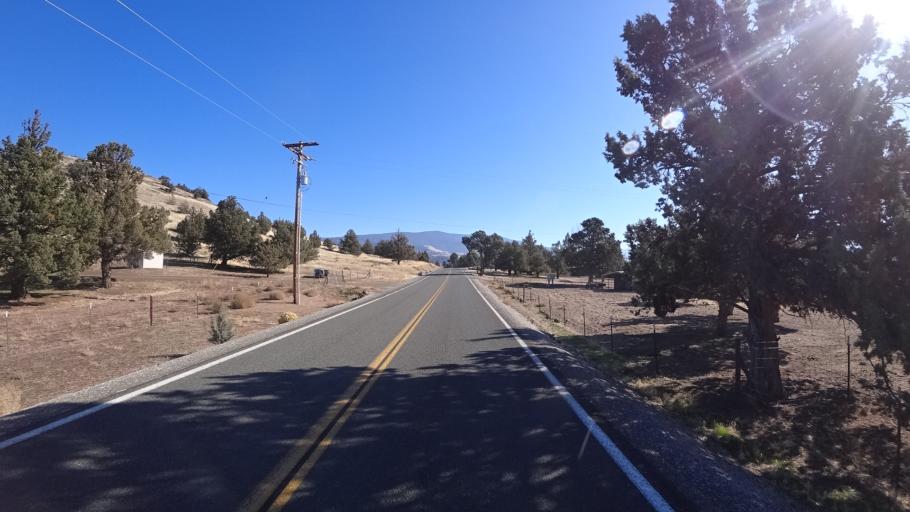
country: US
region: California
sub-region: Siskiyou County
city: Montague
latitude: 41.6592
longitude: -122.3756
